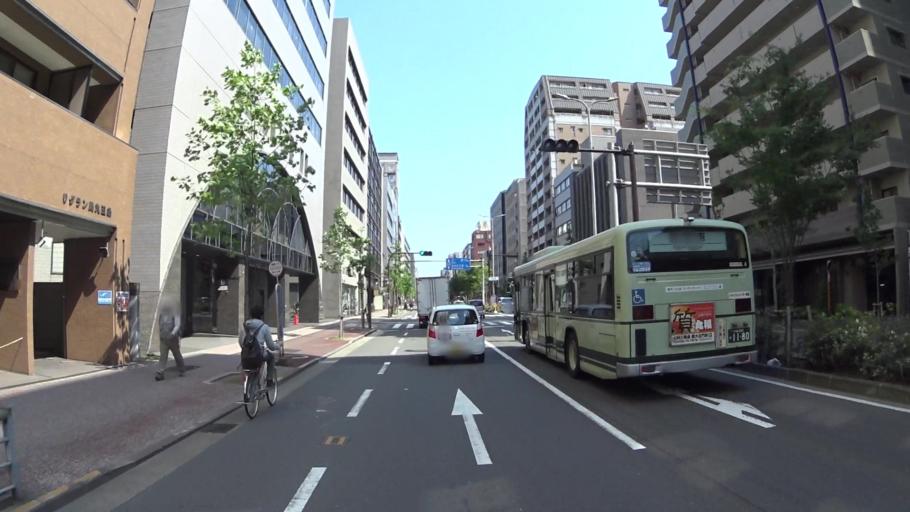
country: JP
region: Kyoto
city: Kyoto
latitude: 34.9975
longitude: 135.7593
